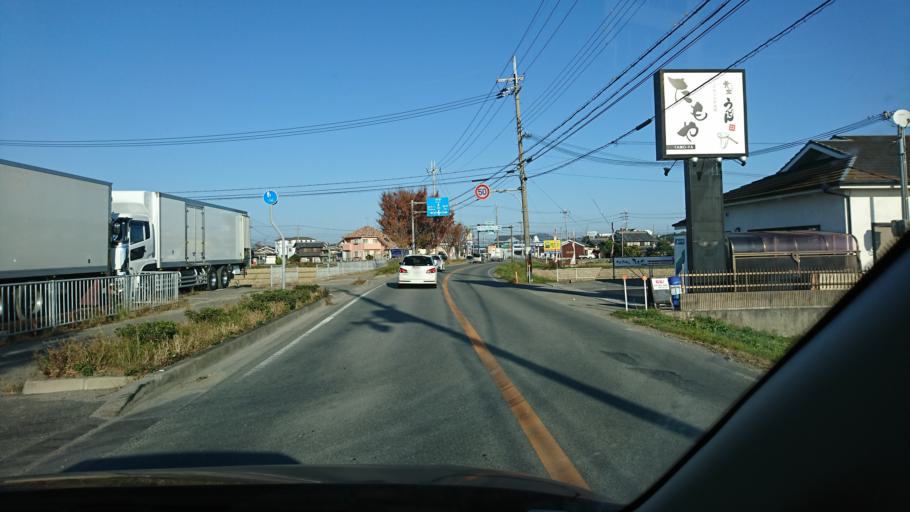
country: JP
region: Hyogo
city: Kakogawacho-honmachi
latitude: 34.7610
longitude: 134.8859
